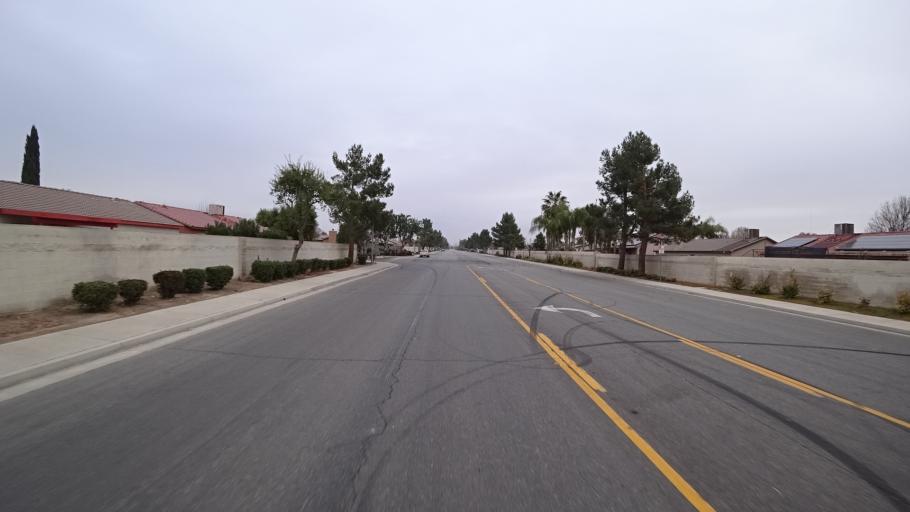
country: US
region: California
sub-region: Kern County
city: Bakersfield
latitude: 35.3470
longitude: -118.9451
